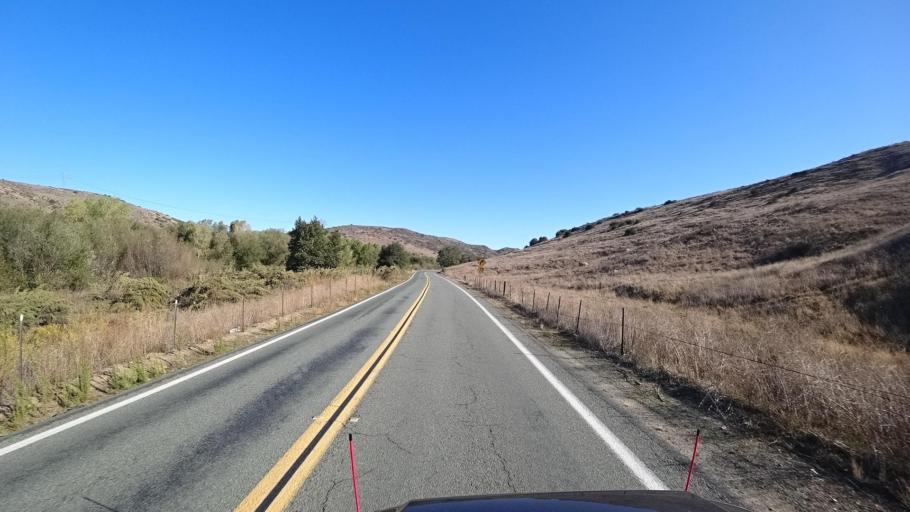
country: US
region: California
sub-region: San Diego County
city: Jamul
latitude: 32.6550
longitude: -116.8480
